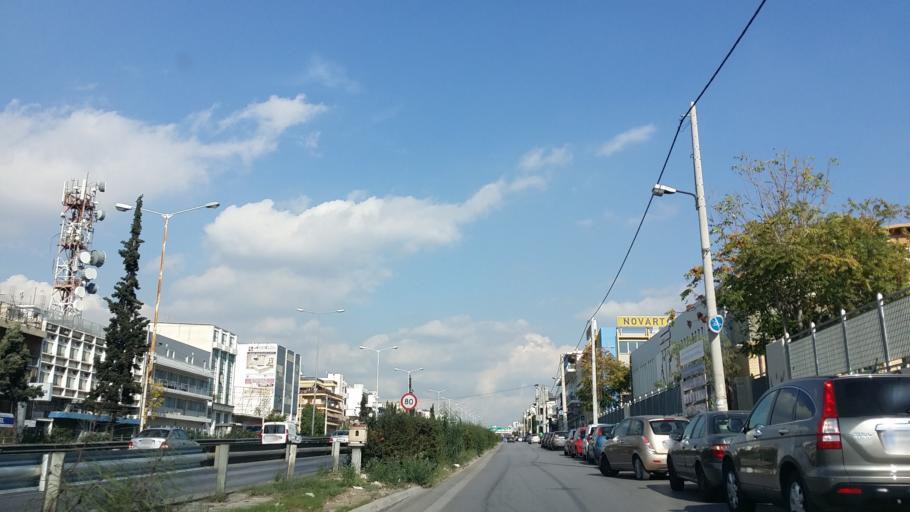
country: GR
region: Attica
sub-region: Nomarchia Athinas
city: Nea Filadelfeia
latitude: 38.0454
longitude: 23.7380
